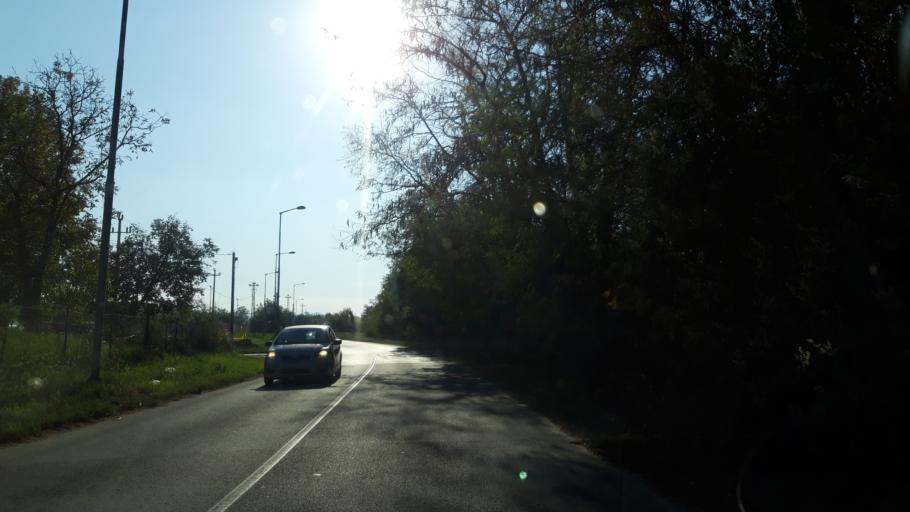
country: RS
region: Autonomna Pokrajina Vojvodina
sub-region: Juznobacki Okrug
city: Petrovaradin
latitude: 45.2340
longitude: 19.8606
